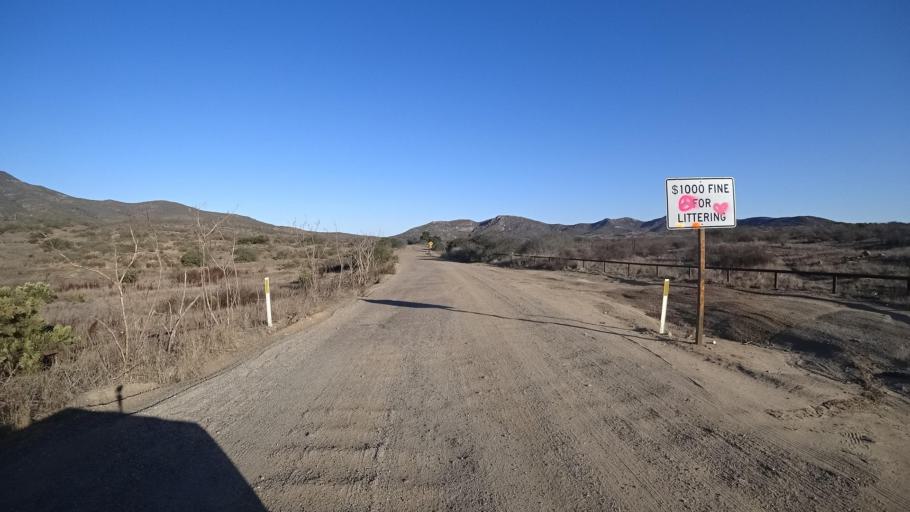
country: US
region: California
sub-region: San Diego County
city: Jamul
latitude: 32.6955
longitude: -116.9041
